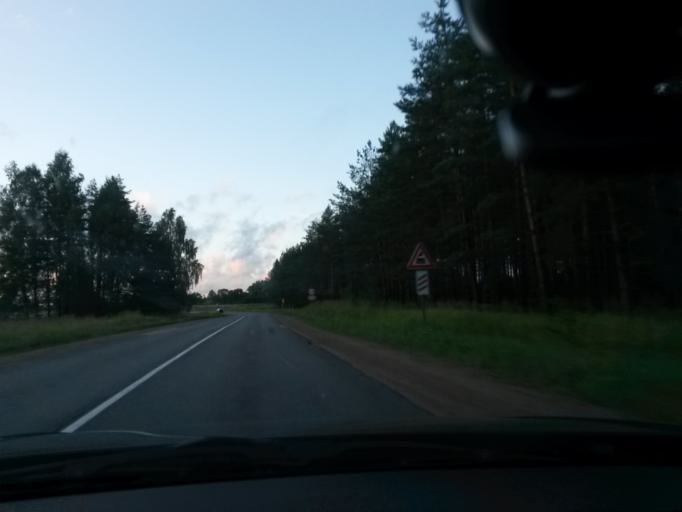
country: LV
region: Jekabpils Rajons
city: Jekabpils
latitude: 56.6873
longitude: 25.9862
